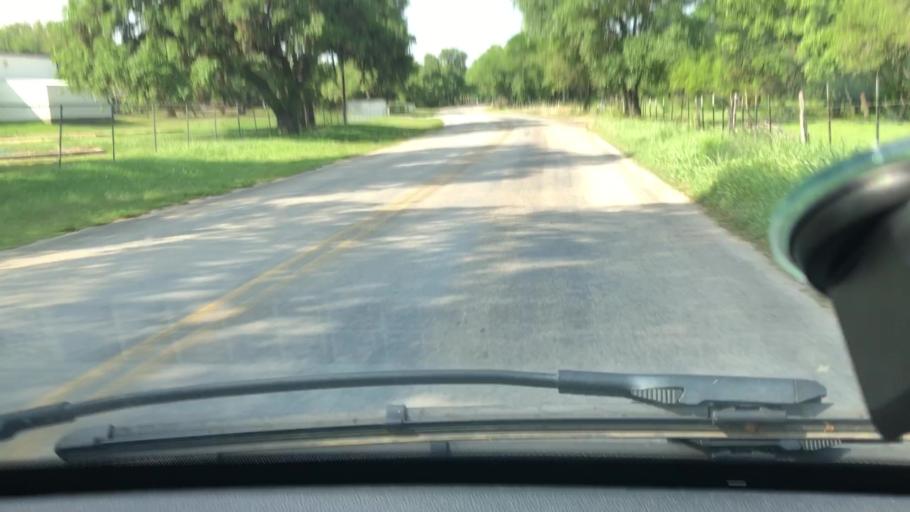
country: US
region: Texas
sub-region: Comal County
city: Bulverde
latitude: 29.7599
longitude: -98.4587
